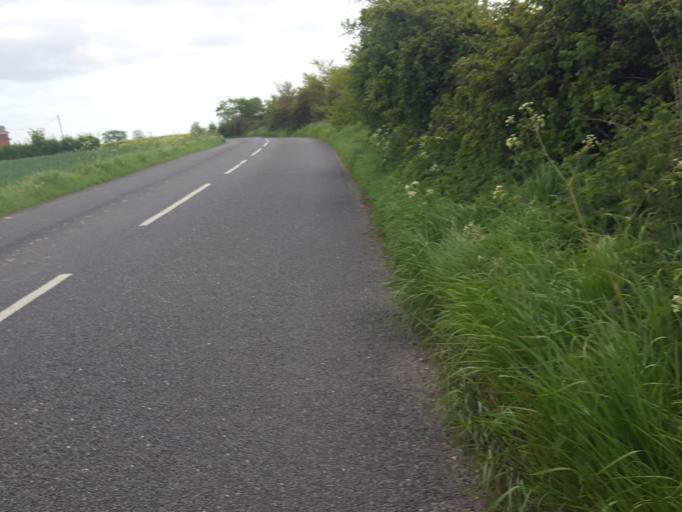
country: GB
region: England
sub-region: Essex
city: Little Clacton
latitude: 51.8213
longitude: 1.1835
